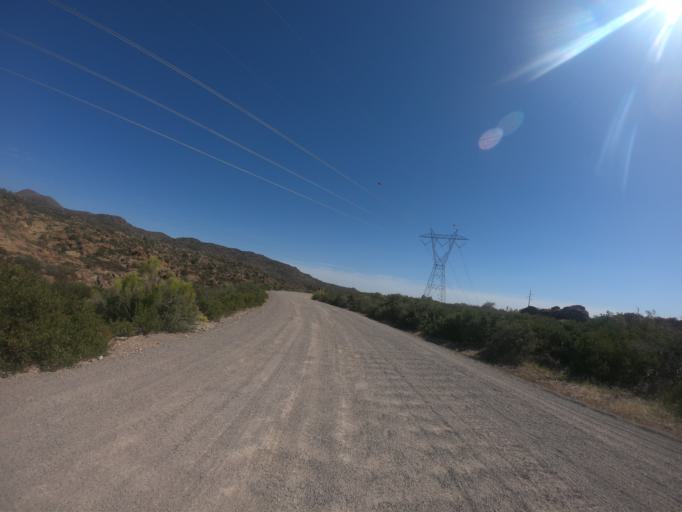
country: US
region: Arizona
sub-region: Pinal County
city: Superior
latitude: 33.3251
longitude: -111.0398
